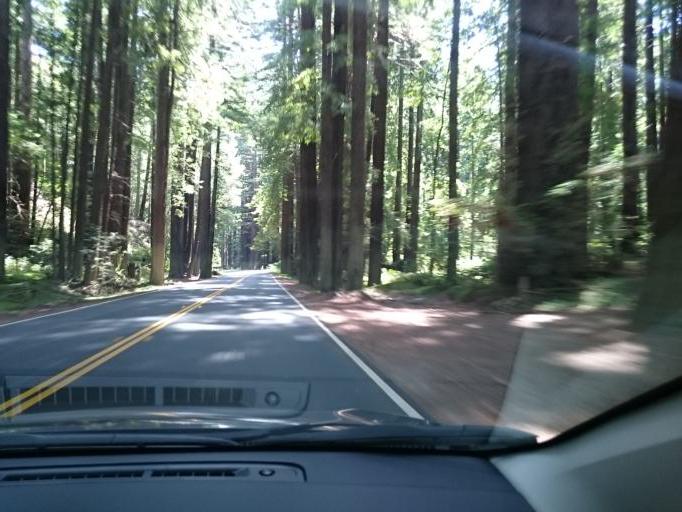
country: US
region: California
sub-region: Mendocino County
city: Fort Bragg
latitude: 39.1619
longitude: -123.6539
